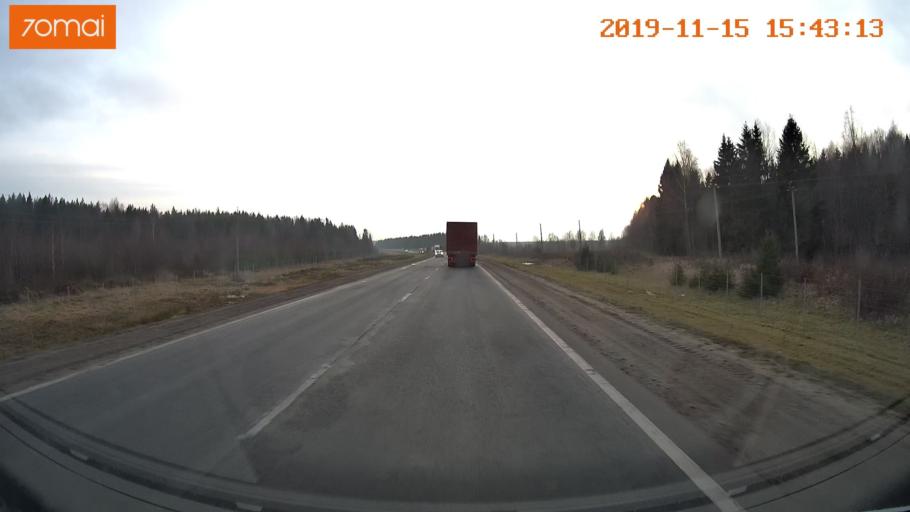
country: RU
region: Jaroslavl
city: Danilov
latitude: 57.9848
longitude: 40.0302
